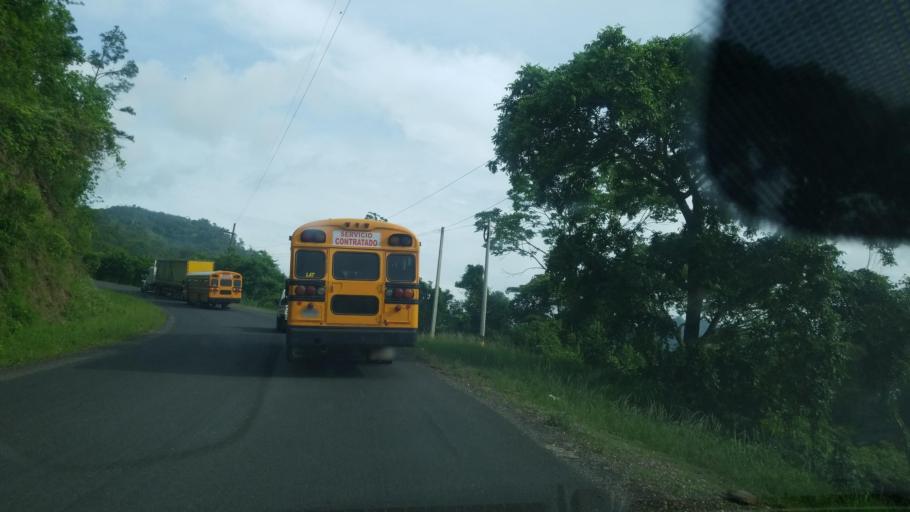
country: HN
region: Santa Barbara
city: Petoa
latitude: 15.2123
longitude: -88.2703
